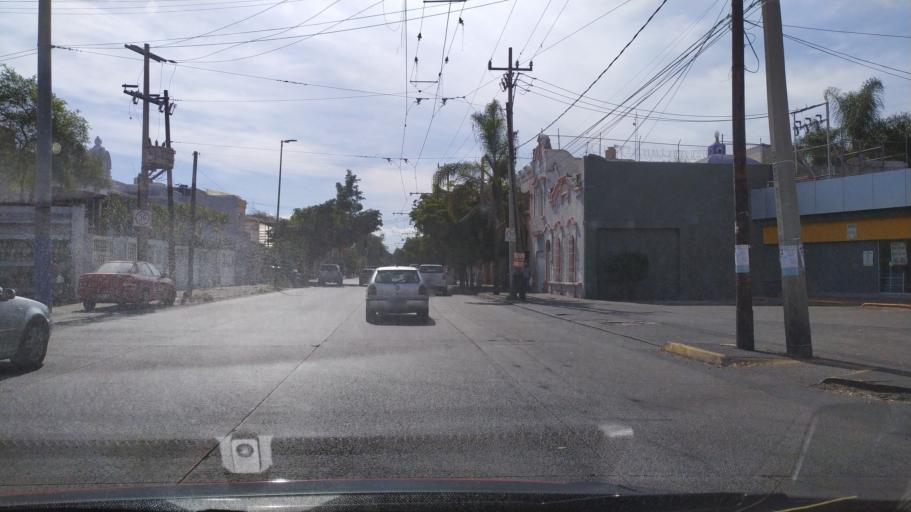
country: MX
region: Jalisco
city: Tlaquepaque
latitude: 20.6778
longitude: -103.3287
